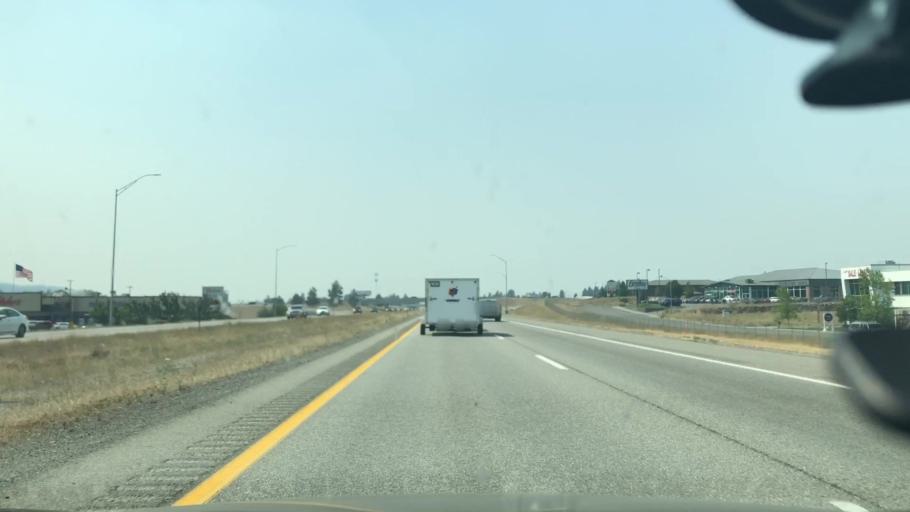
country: US
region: Idaho
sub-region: Kootenai County
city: Post Falls
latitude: 47.7127
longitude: -116.9227
